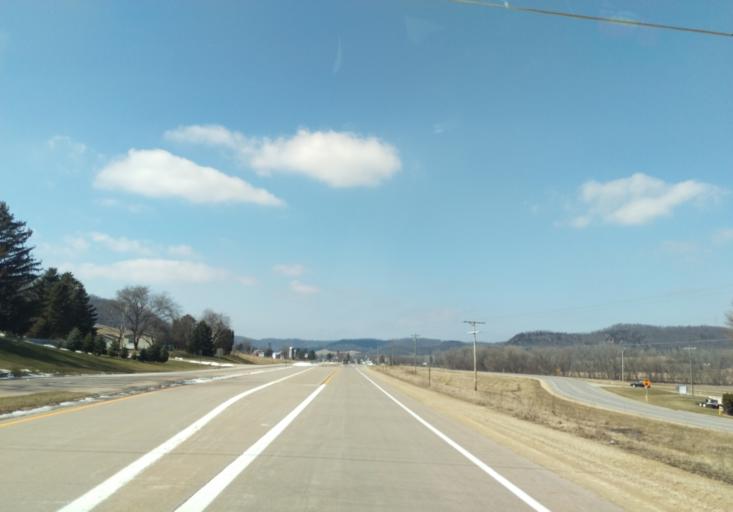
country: US
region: Wisconsin
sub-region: La Crosse County
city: La Crosse
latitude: 43.7538
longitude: -91.1194
